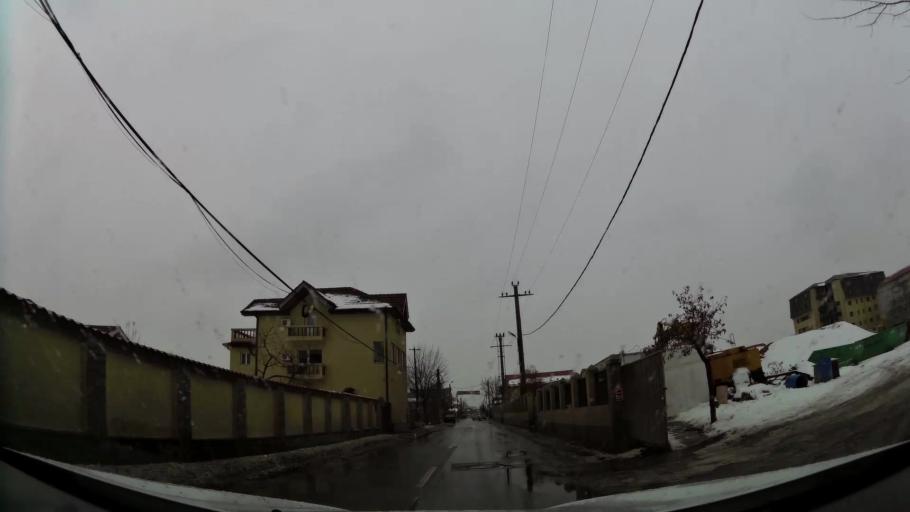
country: RO
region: Ilfov
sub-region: Comuna Bragadiru
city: Bragadiru
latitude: 44.4021
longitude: 26.0110
